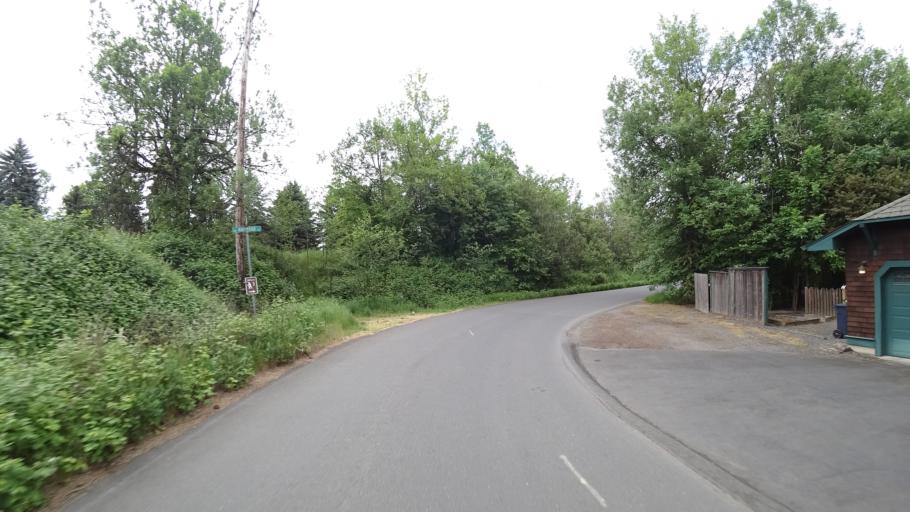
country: US
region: Oregon
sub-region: Washington County
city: Garden Home-Whitford
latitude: 45.4674
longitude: -122.7471
